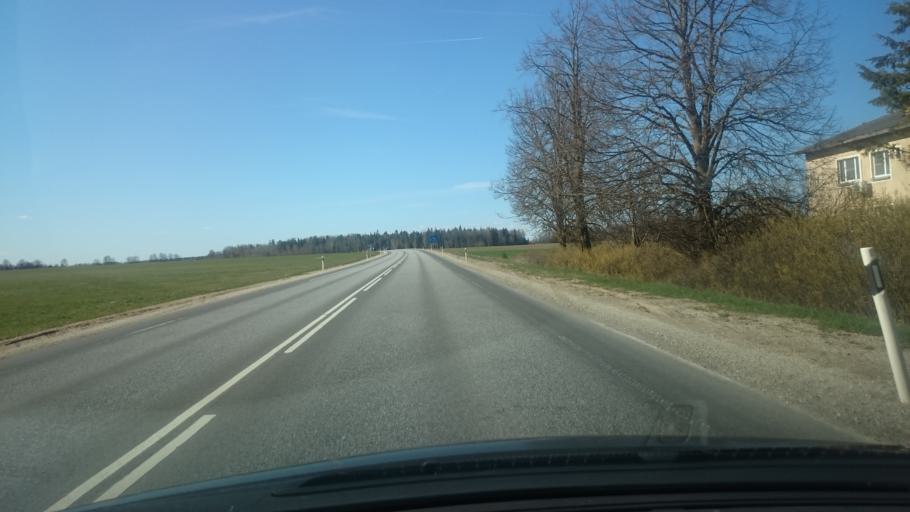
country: EE
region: Tartu
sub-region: Tartu linn
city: Tartu
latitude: 58.3631
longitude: 26.8894
